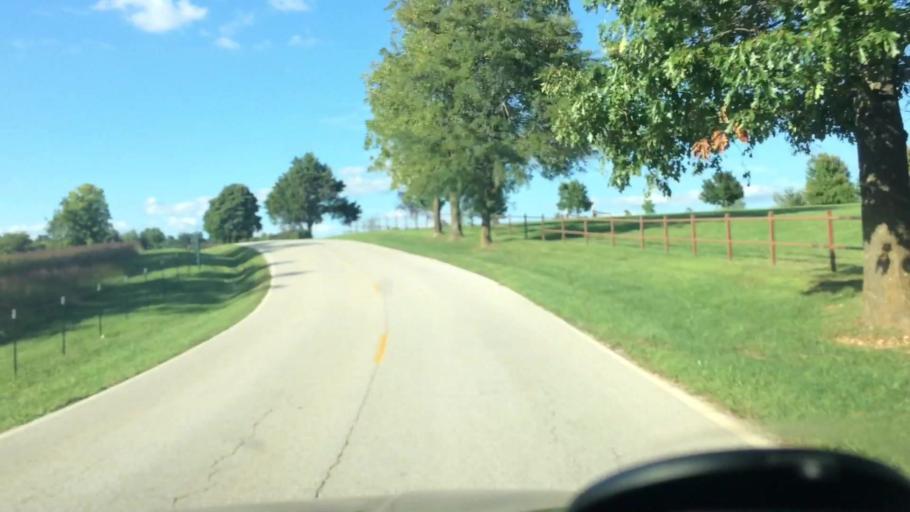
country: US
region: Missouri
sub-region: Greene County
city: Strafford
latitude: 37.2750
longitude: -93.0807
